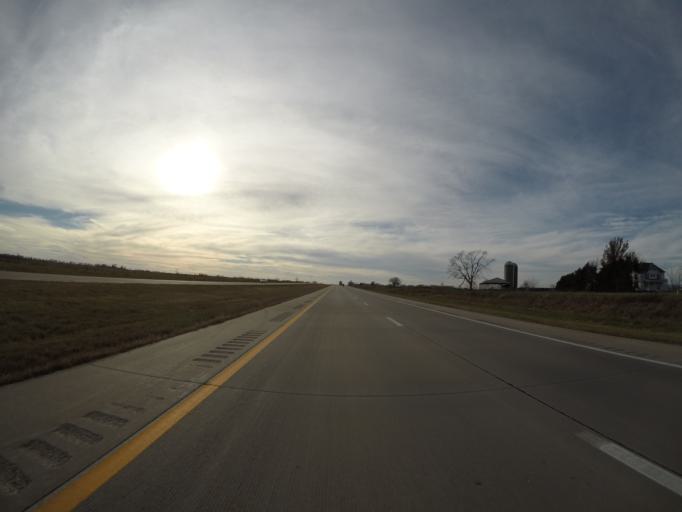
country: US
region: Kansas
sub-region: Franklin County
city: Wellsville
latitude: 38.7018
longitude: -95.0851
